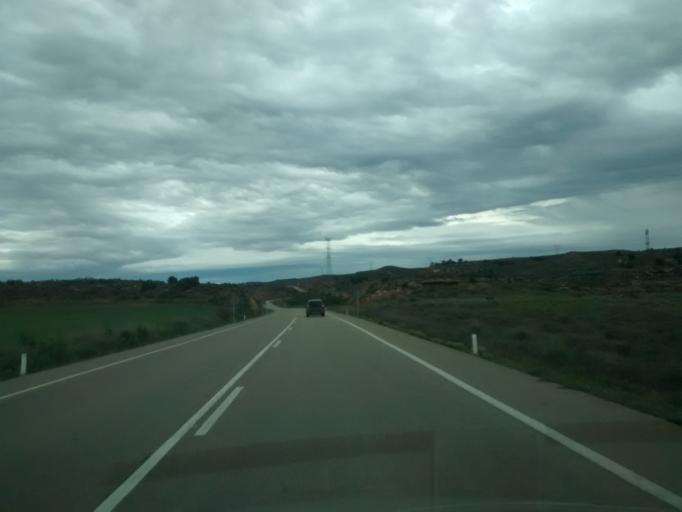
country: ES
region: Aragon
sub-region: Provincia de Zaragoza
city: Caspe
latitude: 41.1908
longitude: 0.0464
